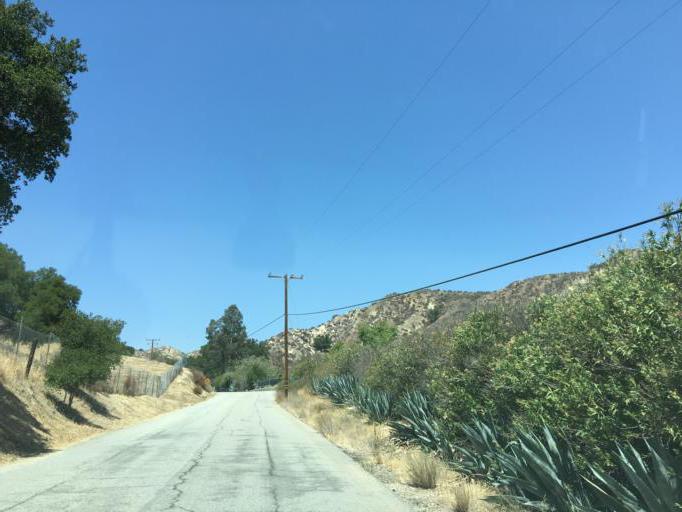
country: US
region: California
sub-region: Los Angeles County
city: Val Verde
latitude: 34.4507
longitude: -118.6829
